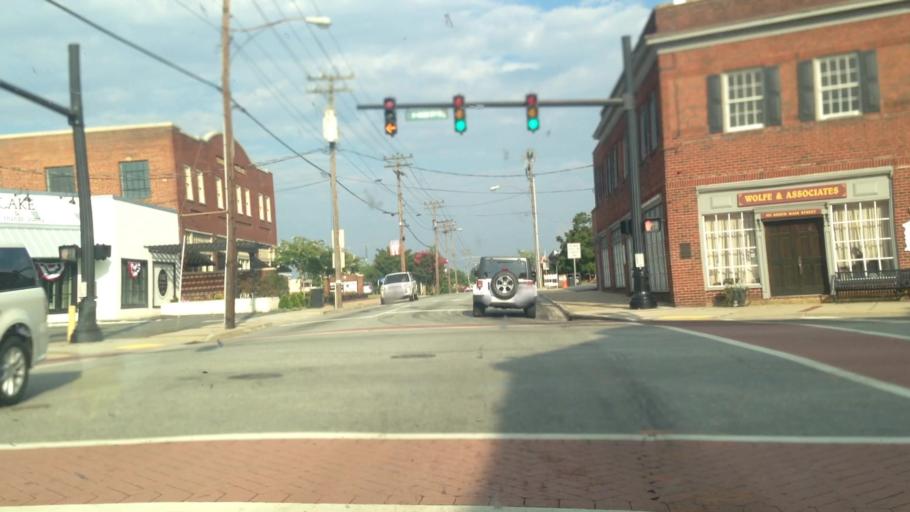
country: US
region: North Carolina
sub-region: Forsyth County
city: Kernersville
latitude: 36.1198
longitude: -80.0734
